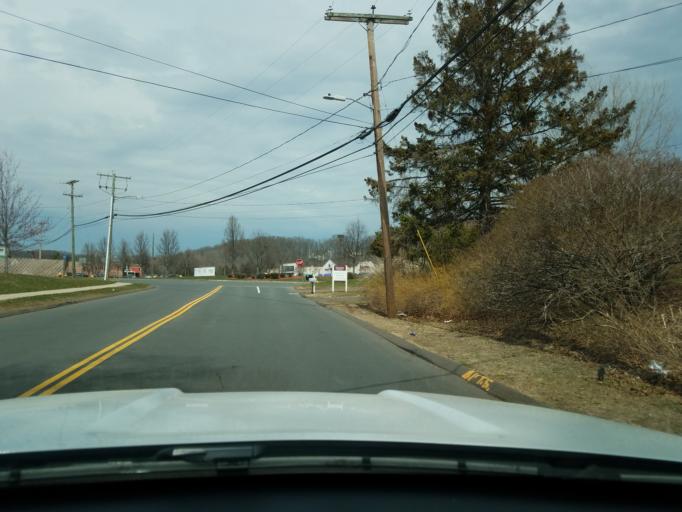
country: US
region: Connecticut
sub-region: Hartford County
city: Newington
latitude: 41.6805
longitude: -72.7096
